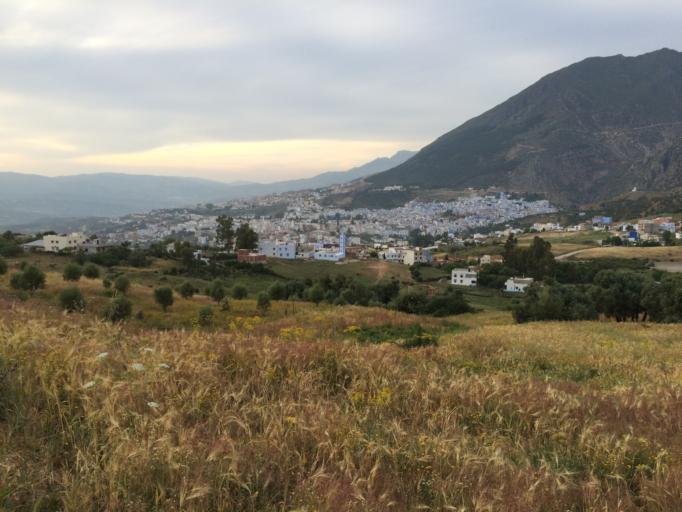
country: MA
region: Tanger-Tetouan
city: Chefchaouene
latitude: 35.1485
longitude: -5.2588
